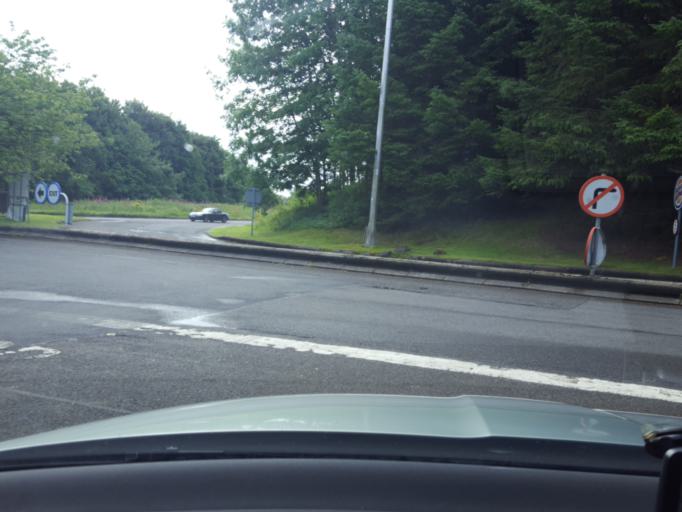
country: GB
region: Scotland
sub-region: Stirling
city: Bannockburn
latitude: 56.0768
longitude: -3.9214
